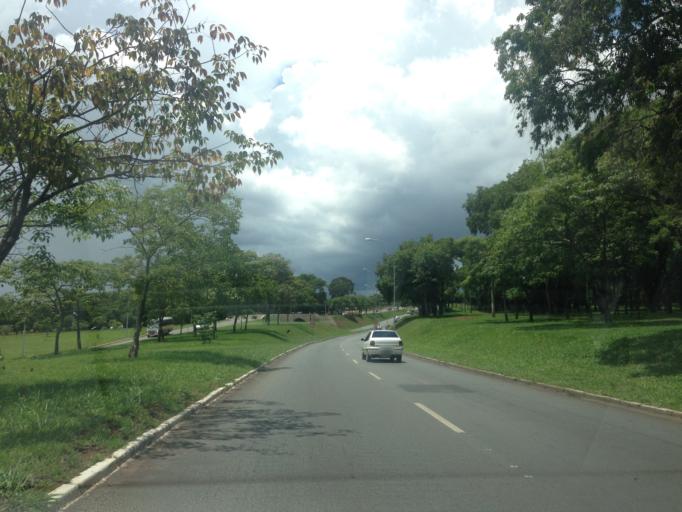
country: BR
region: Federal District
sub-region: Brasilia
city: Brasilia
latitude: -15.8338
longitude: -47.9261
